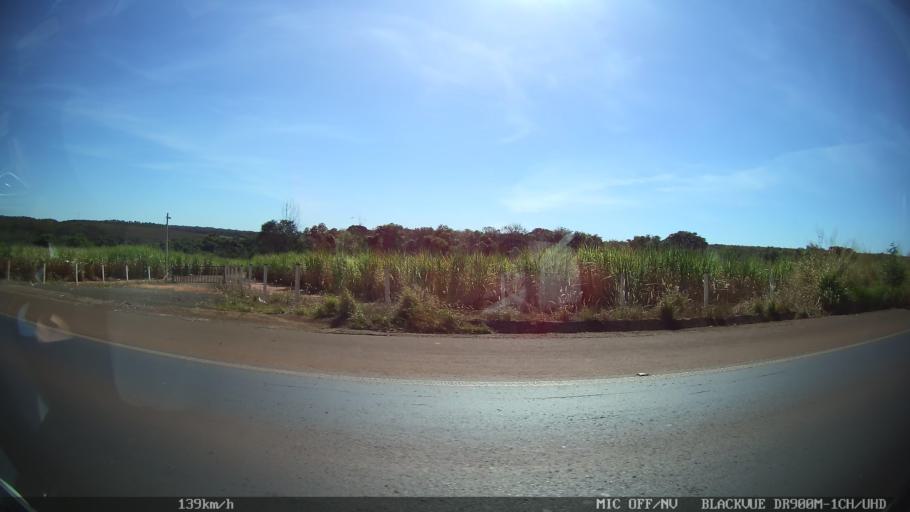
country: BR
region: Sao Paulo
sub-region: Barretos
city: Barretos
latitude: -20.5205
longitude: -48.5779
